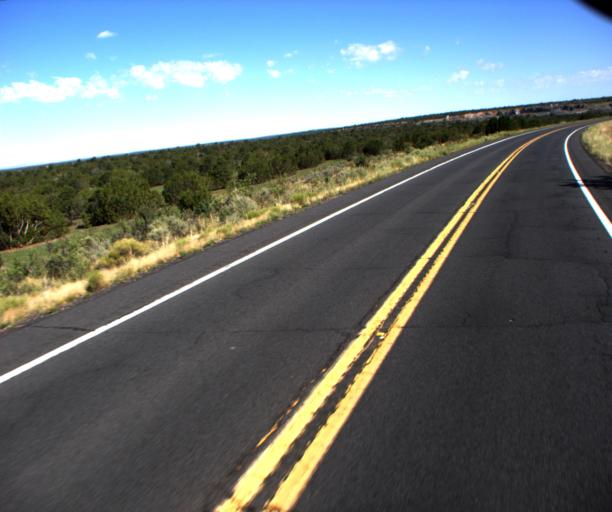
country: US
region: Arizona
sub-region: Coconino County
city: Williams
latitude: 35.4751
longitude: -112.1772
